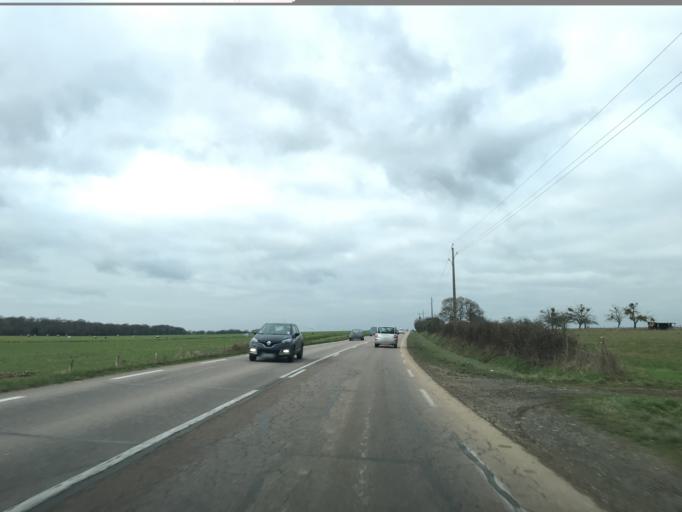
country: FR
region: Haute-Normandie
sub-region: Departement de l'Eure
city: Fleury-sur-Andelle
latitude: 49.3731
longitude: 1.3336
